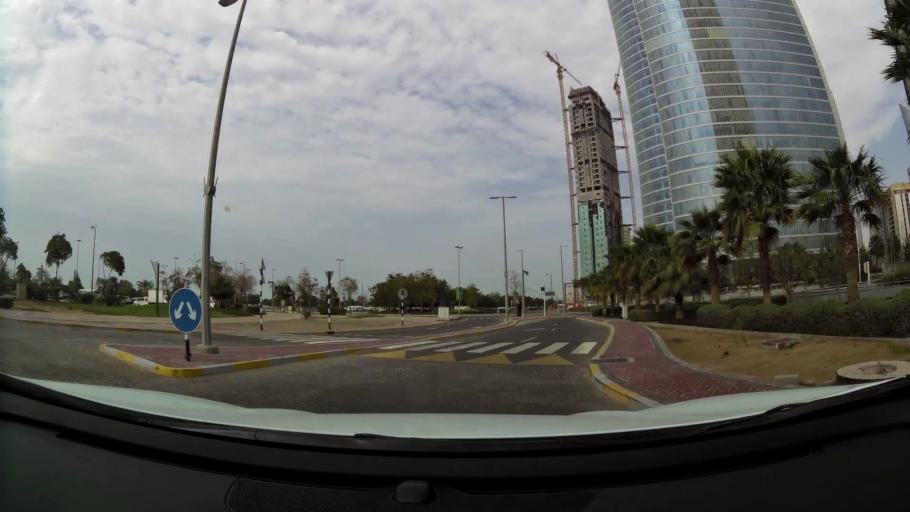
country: AE
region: Abu Dhabi
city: Abu Dhabi
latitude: 24.4853
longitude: 54.3503
